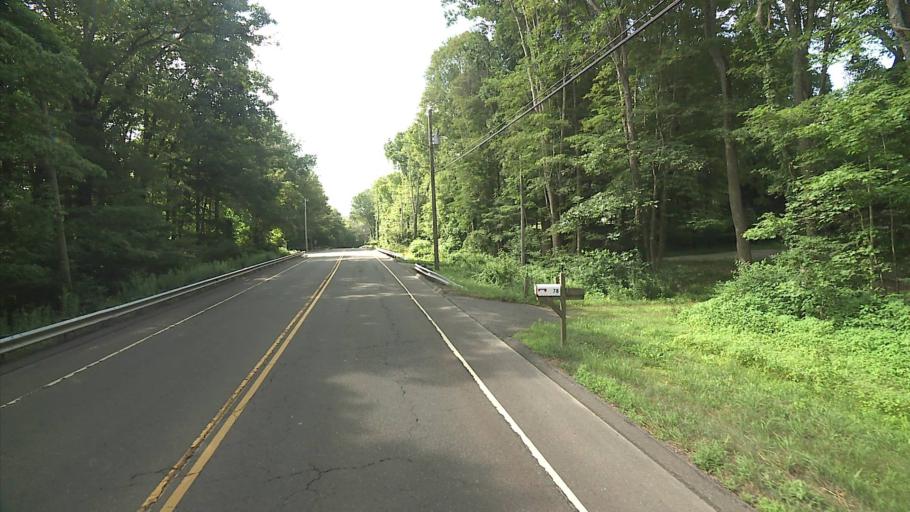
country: US
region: Connecticut
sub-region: Middlesex County
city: Chester Center
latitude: 41.3540
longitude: -72.4979
